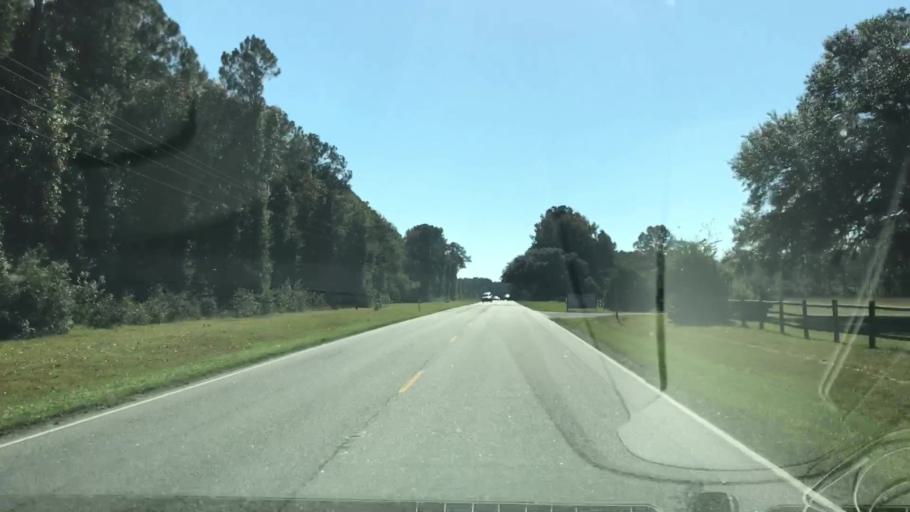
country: US
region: South Carolina
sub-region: Jasper County
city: Ridgeland
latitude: 32.4487
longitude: -80.8978
